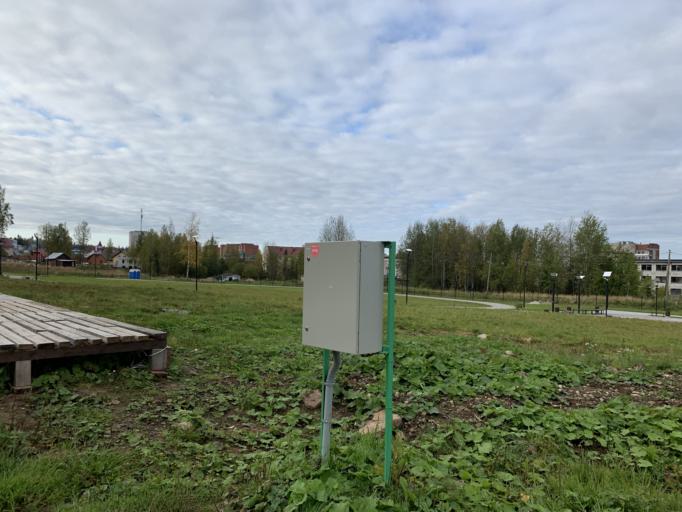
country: RU
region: Perm
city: Gubakha
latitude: 58.8333
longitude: 57.5622
